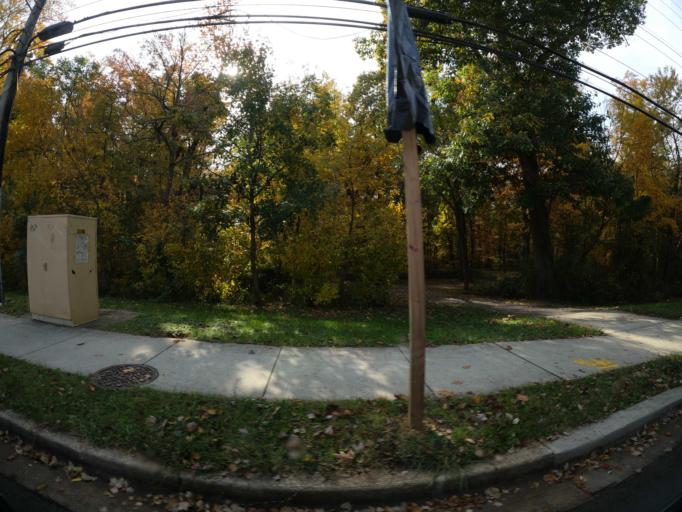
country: US
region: Maryland
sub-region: Prince George's County
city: College Park
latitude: 38.9894
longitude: -76.9324
